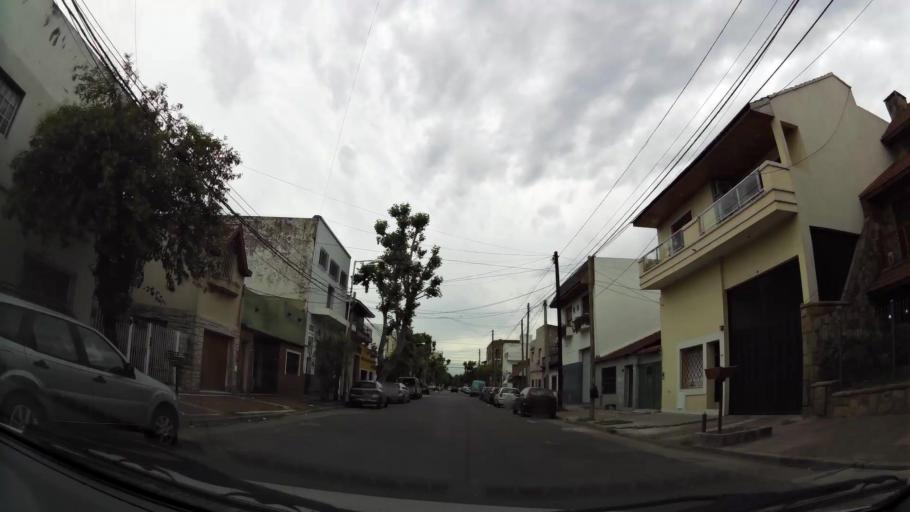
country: AR
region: Buenos Aires
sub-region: Partido de Avellaneda
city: Avellaneda
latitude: -34.6757
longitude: -58.3869
